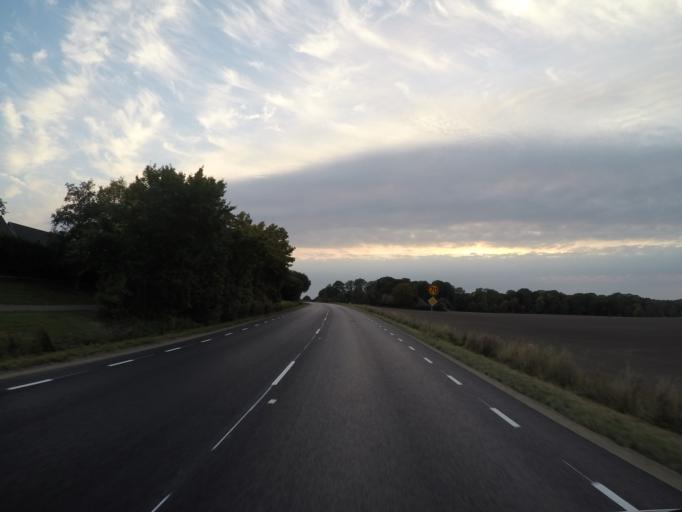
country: SE
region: Skane
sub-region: Lunds Kommun
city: Genarp
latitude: 55.6748
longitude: 13.3428
